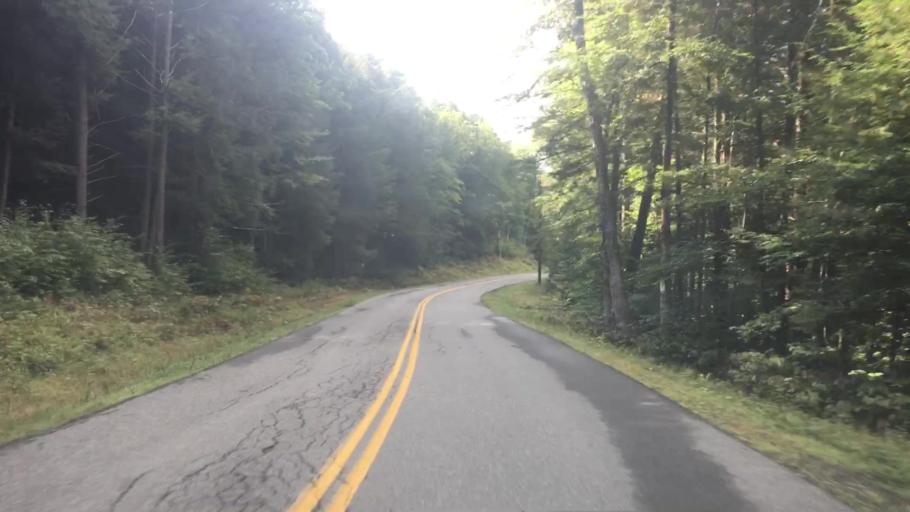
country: US
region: Vermont
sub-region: Windham County
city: Dover
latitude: 42.8102
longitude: -72.7657
